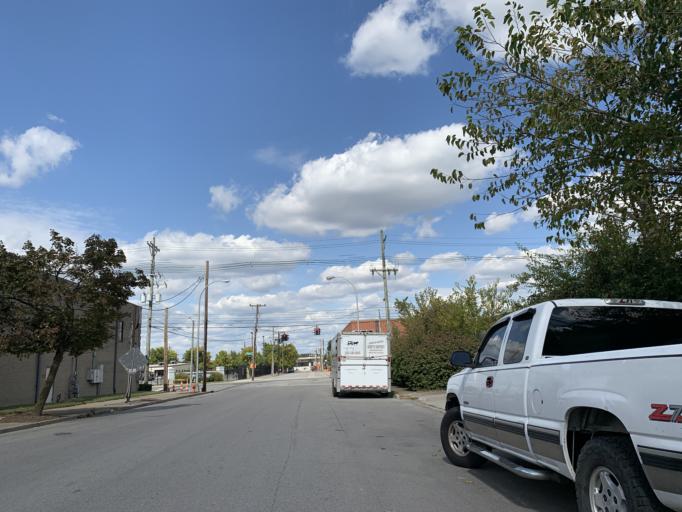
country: US
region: Kentucky
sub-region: Jefferson County
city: Louisville
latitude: 38.2559
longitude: -85.7684
